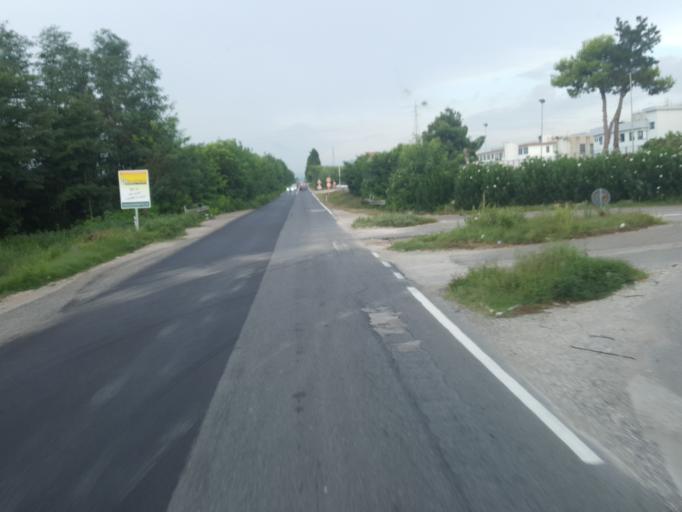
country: IT
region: Campania
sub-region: Provincia di Caserta
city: Pignataro Maggiore
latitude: 41.1673
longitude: 14.1544
